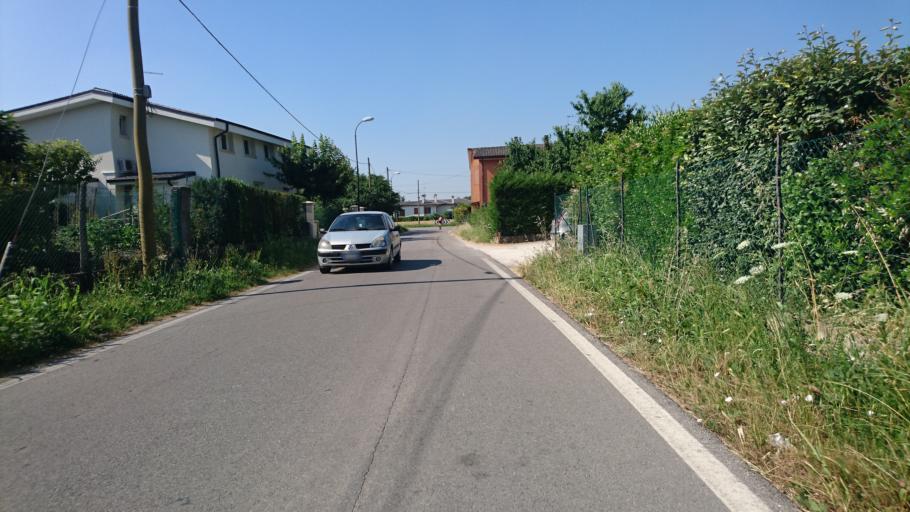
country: IT
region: Veneto
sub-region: Provincia di Padova
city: Abano Terme
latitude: 45.3692
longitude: 11.8091
